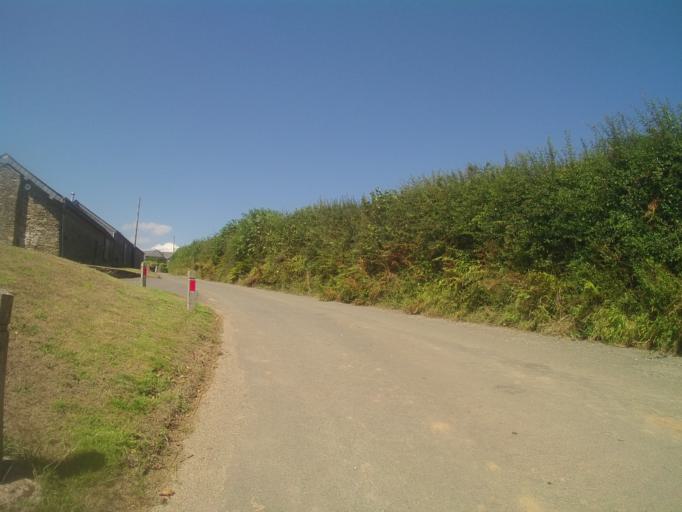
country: GB
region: England
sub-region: Devon
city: Dartmouth
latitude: 50.3641
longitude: -3.6234
